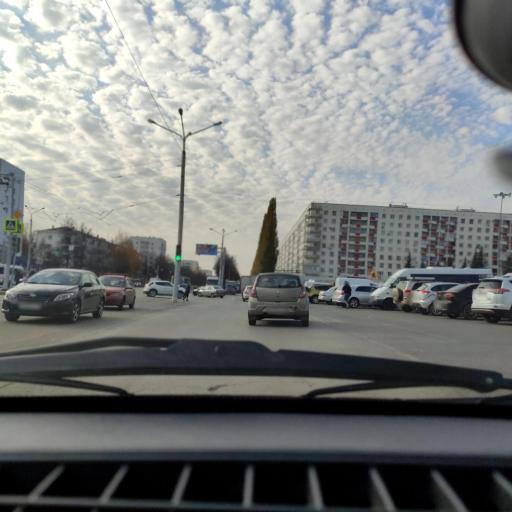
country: RU
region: Bashkortostan
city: Ufa
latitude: 54.7596
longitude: 55.9973
